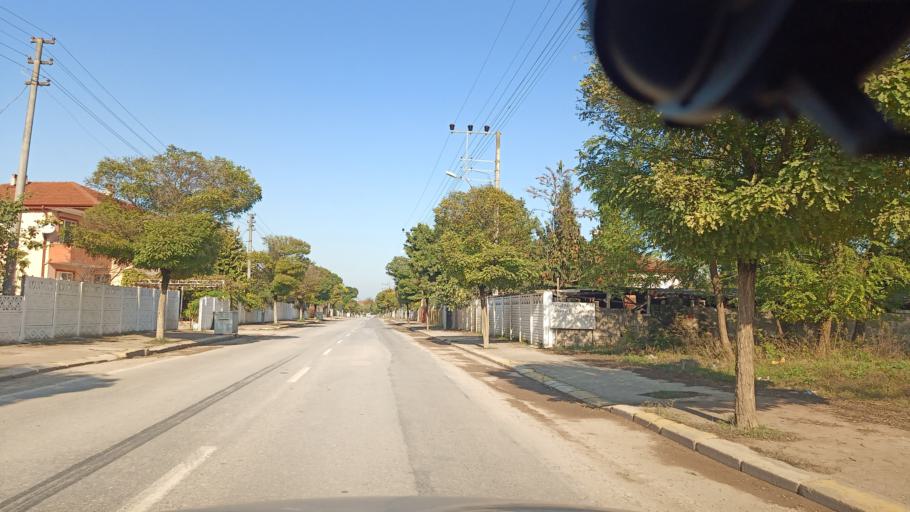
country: TR
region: Sakarya
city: Sogutlu
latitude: 40.8871
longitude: 30.4651
